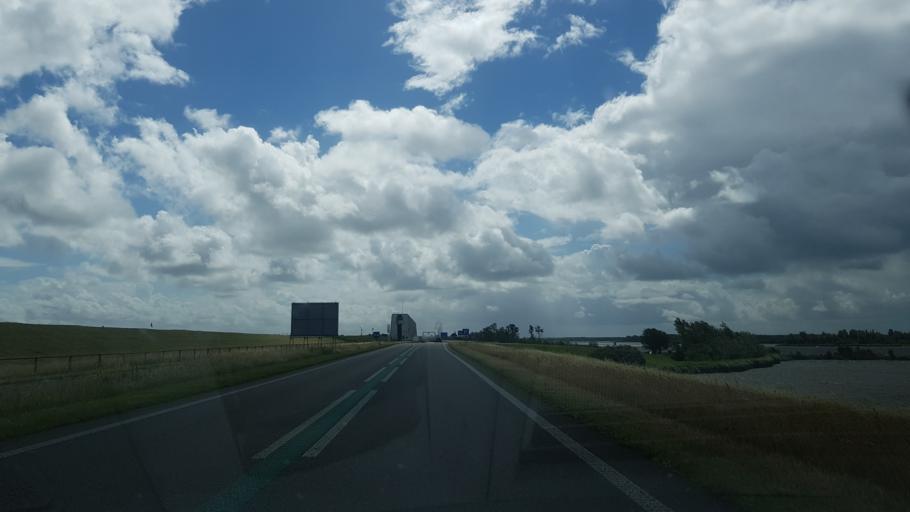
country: NL
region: Friesland
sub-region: Gemeente Dongeradeel
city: Anjum
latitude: 53.4131
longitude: 6.1852
